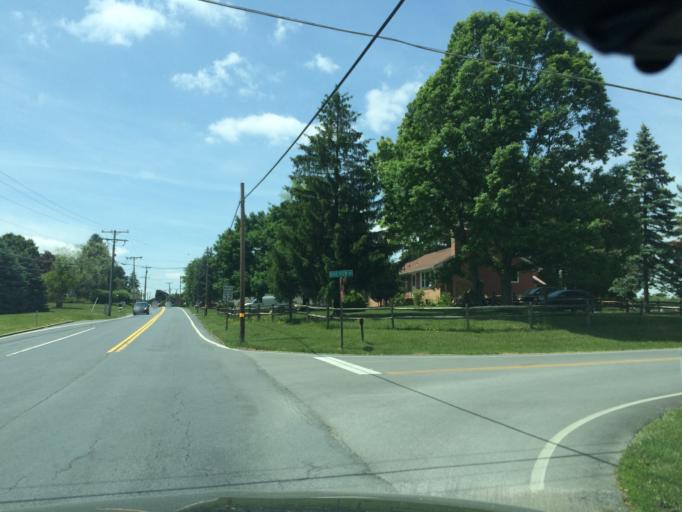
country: US
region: Maryland
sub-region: Carroll County
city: Eldersburg
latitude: 39.4875
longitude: -76.9618
